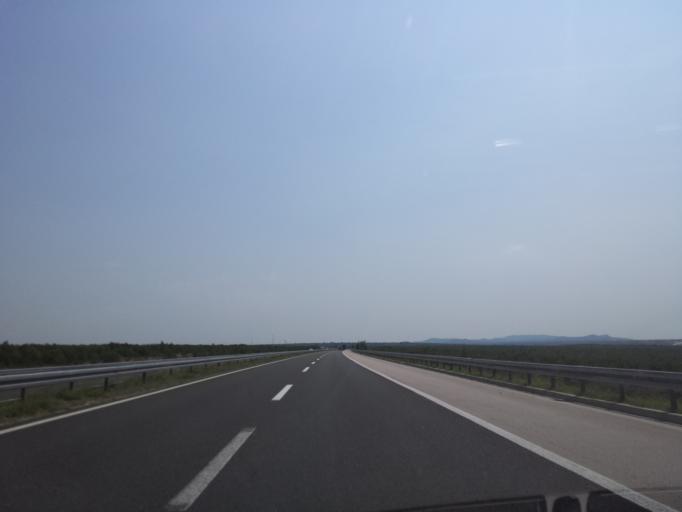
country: HR
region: Zadarska
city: Benkovac
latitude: 44.0309
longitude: 15.5649
